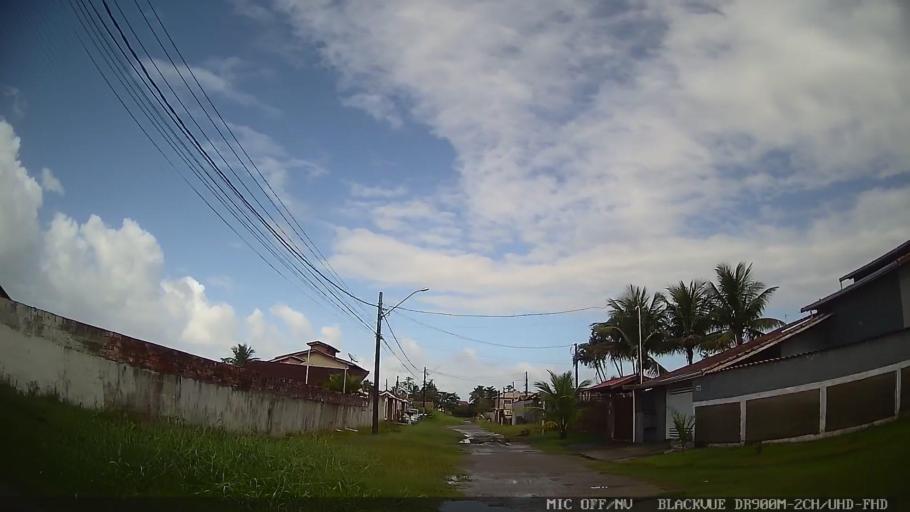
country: BR
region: Sao Paulo
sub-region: Itanhaem
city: Itanhaem
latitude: -24.2078
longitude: -46.8425
